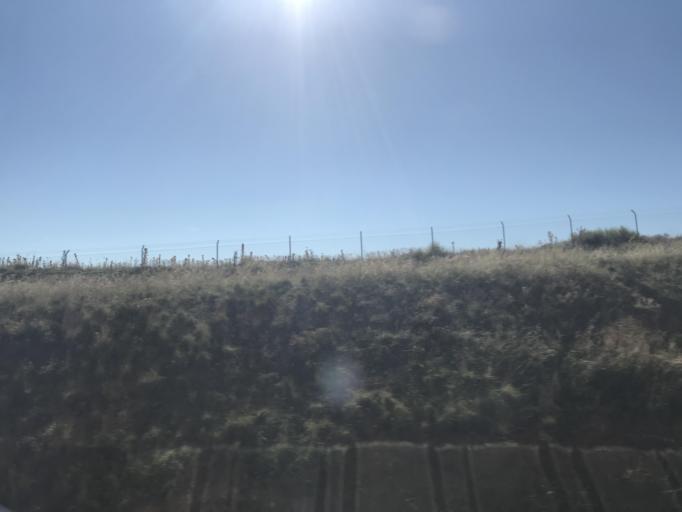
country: ES
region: Madrid
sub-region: Provincia de Madrid
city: Torres de la Alameda
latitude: 40.4287
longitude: -3.3721
